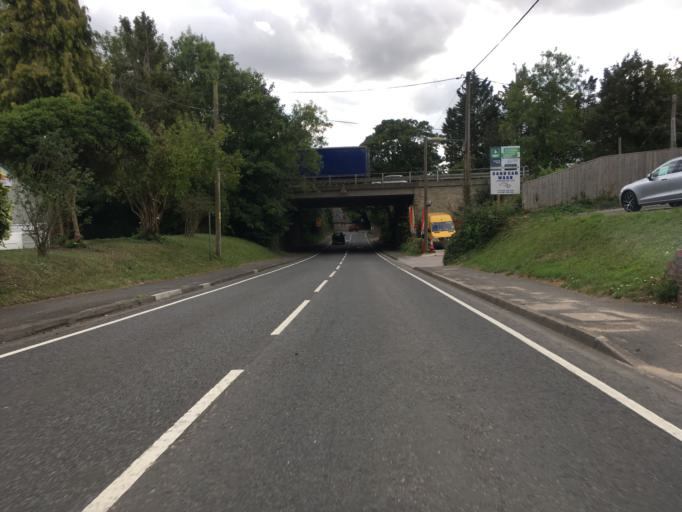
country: GB
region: England
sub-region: Hampshire
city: Kings Worthy
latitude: 51.0877
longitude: -1.3007
